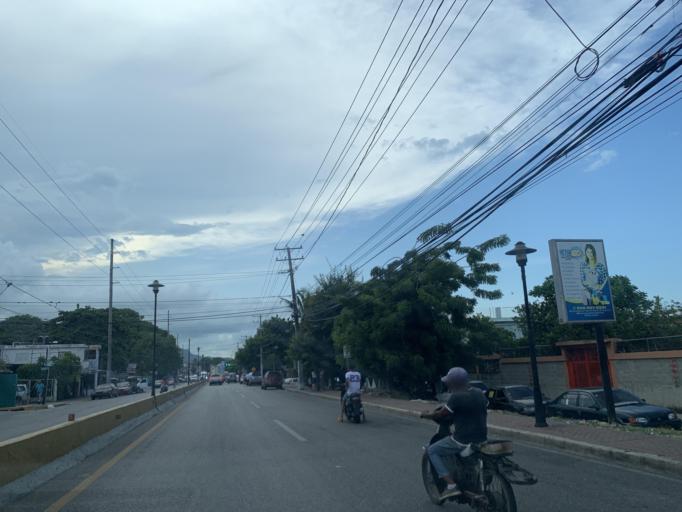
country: DO
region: Puerto Plata
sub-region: Puerto Plata
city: Puerto Plata
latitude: 19.7890
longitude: -70.6983
